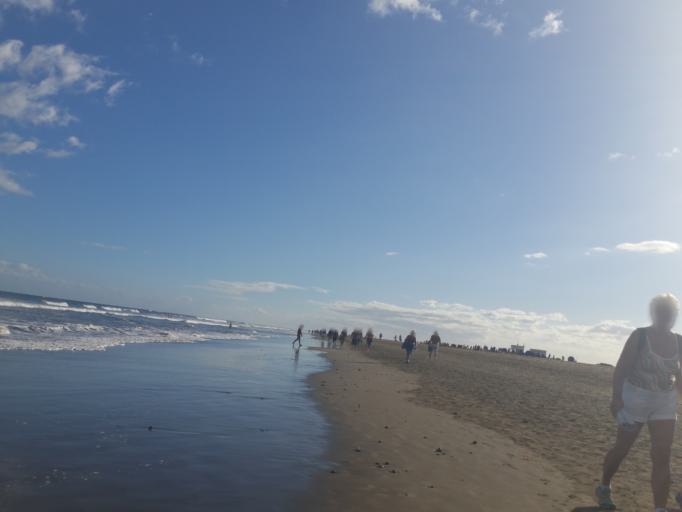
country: ES
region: Canary Islands
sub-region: Provincia de Las Palmas
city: Playa del Ingles
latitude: 27.7456
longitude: -15.5682
